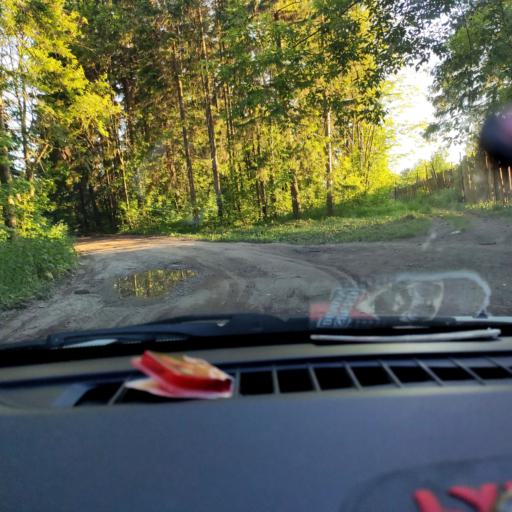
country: RU
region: Perm
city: Froly
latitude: 57.9427
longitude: 56.1986
